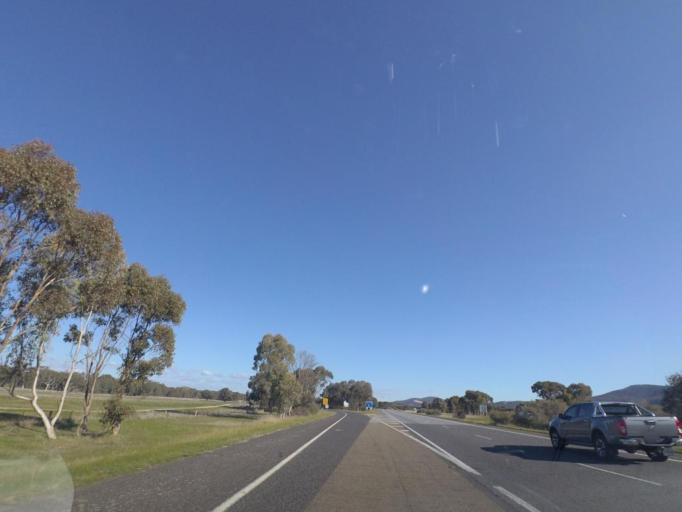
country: AU
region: Victoria
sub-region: Wangaratta
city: Wangaratta
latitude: -36.4213
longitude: 146.2641
